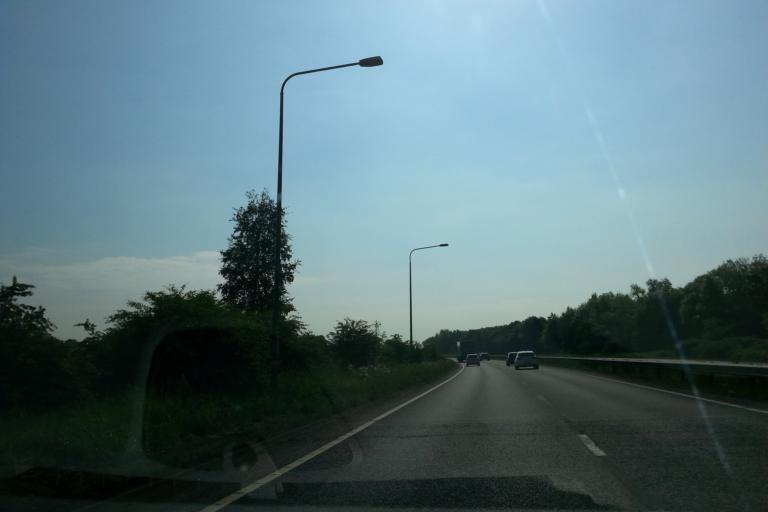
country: GB
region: England
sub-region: Peterborough
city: Upton
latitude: 52.5798
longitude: -0.3756
